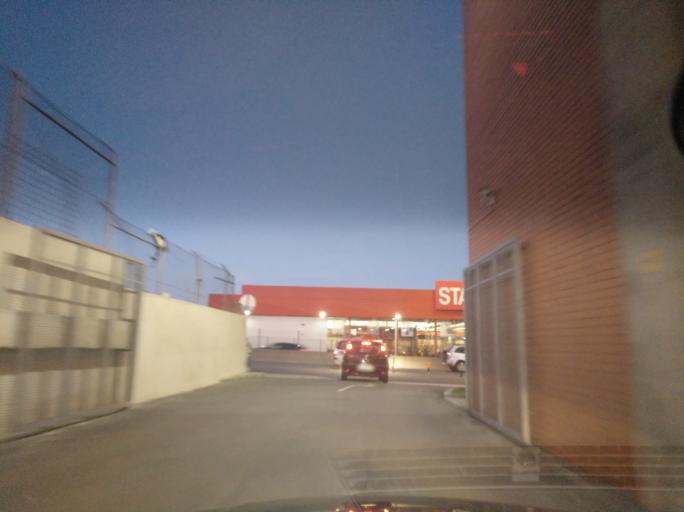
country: PT
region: Lisbon
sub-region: Loures
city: Moscavide
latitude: 38.7557
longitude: -9.1042
